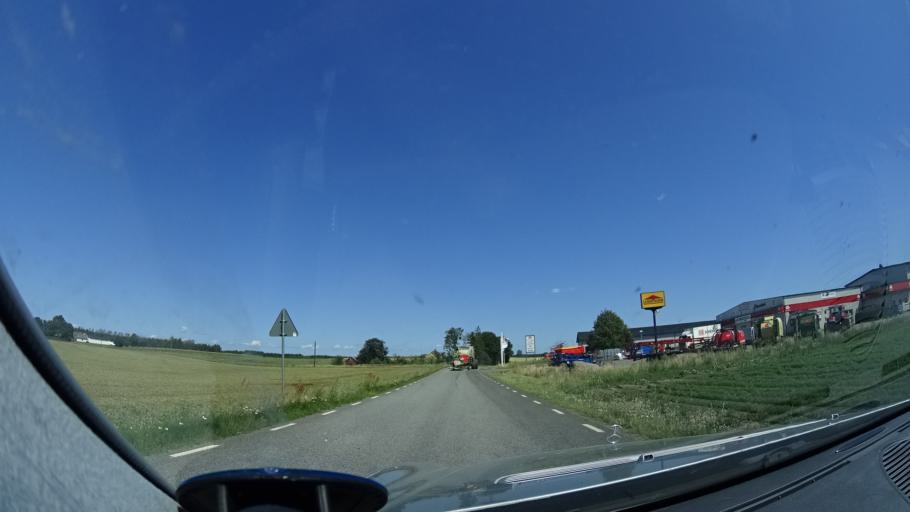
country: SE
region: Skane
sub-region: Kristianstads Kommun
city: Degeberga
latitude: 55.8917
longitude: 14.0401
